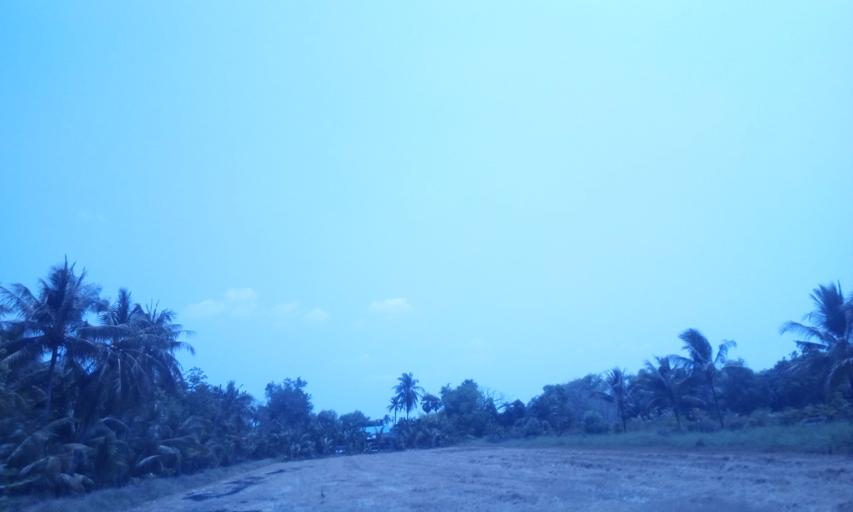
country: TH
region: Chachoengsao
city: Bang Nam Priao
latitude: 13.8834
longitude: 100.9691
